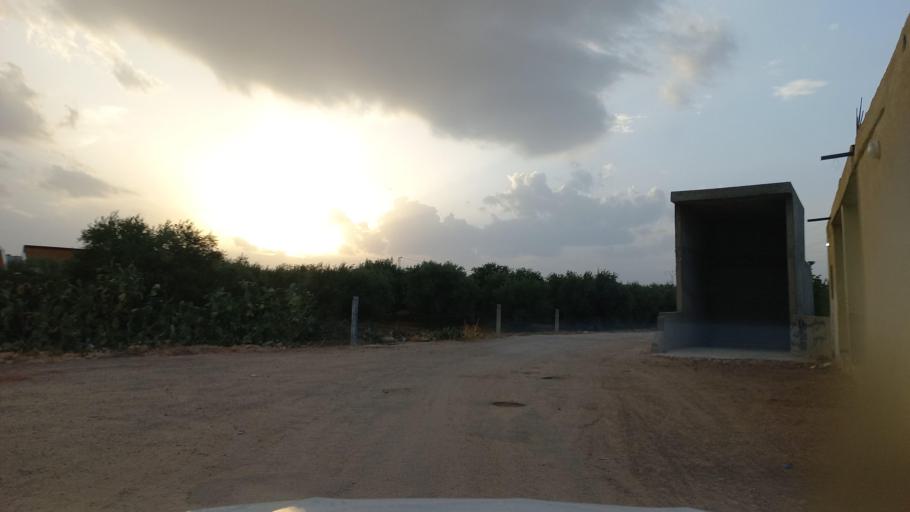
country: TN
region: Al Qasrayn
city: Kasserine
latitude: 35.2716
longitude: 9.0550
